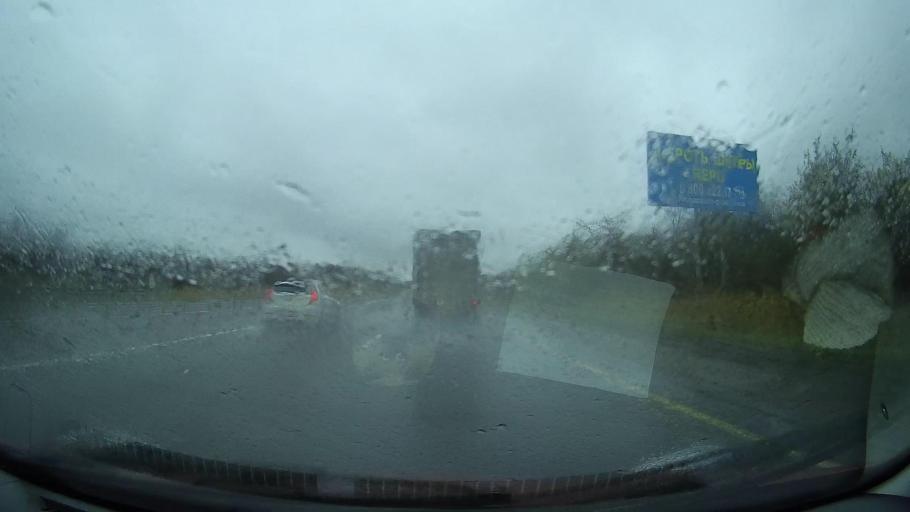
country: RU
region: Stavropol'skiy
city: Nevinnomyssk
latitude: 44.6382
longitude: 41.9836
